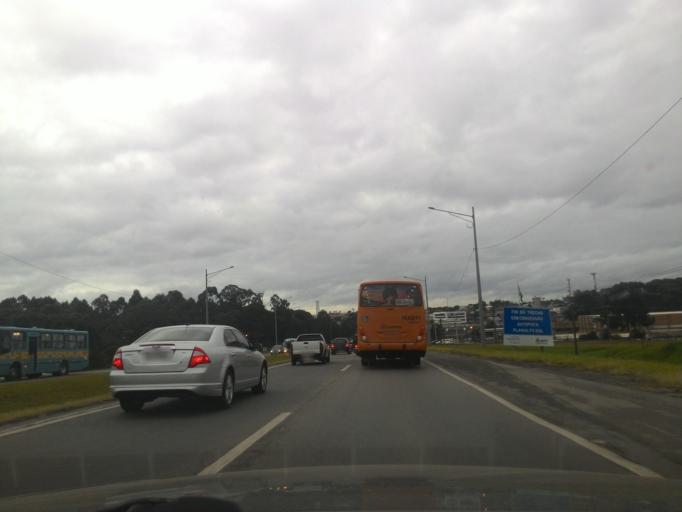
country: BR
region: Parana
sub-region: Sao Jose Dos Pinhais
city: Sao Jose dos Pinhais
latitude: -25.5429
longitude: -49.3028
